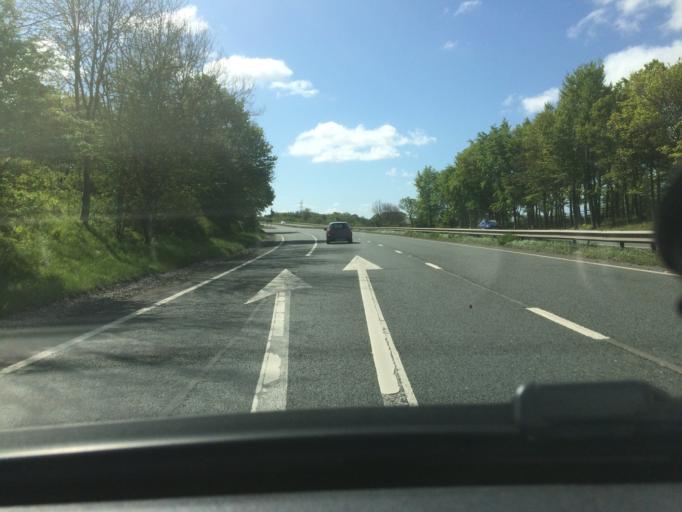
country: GB
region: Wales
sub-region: Wrexham
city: Rhosllanerchrugog
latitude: 53.0303
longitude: -3.0321
